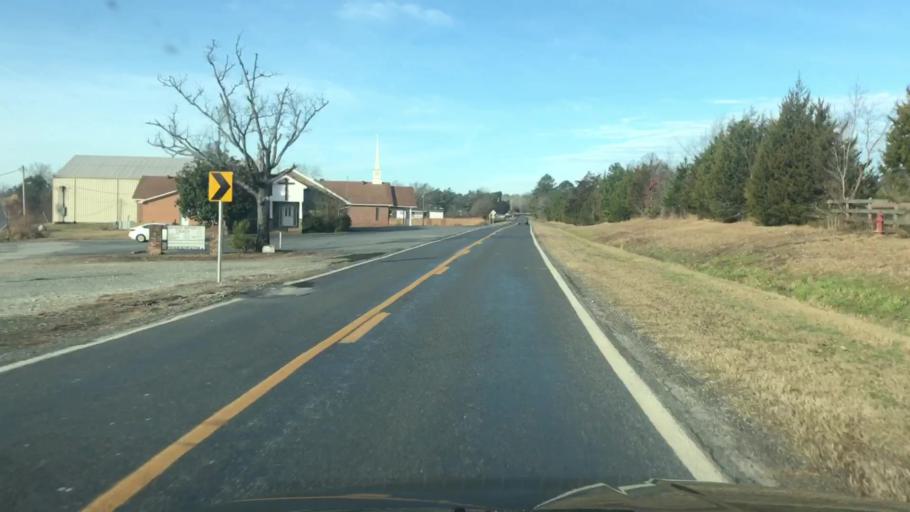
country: US
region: Arkansas
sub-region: Garland County
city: Rockwell
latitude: 34.4711
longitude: -93.2463
